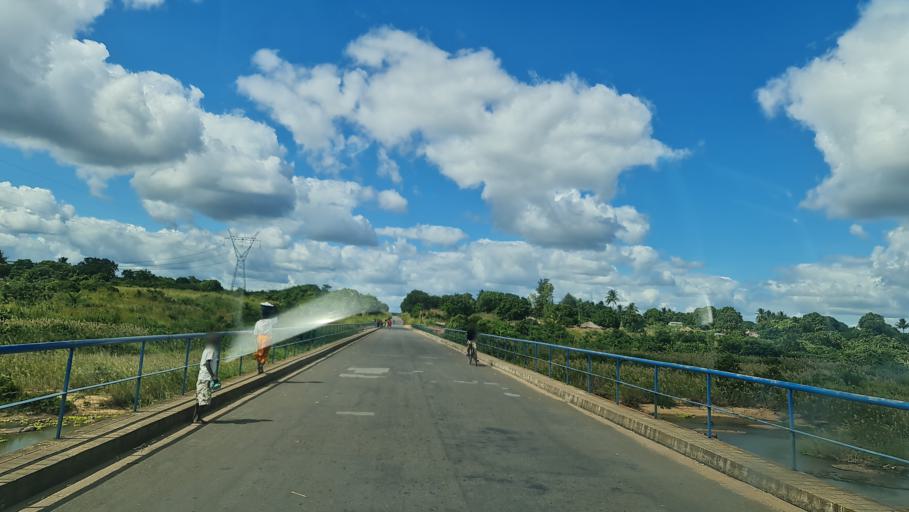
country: MZ
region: Zambezia
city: Quelimane
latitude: -17.5251
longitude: 36.2726
